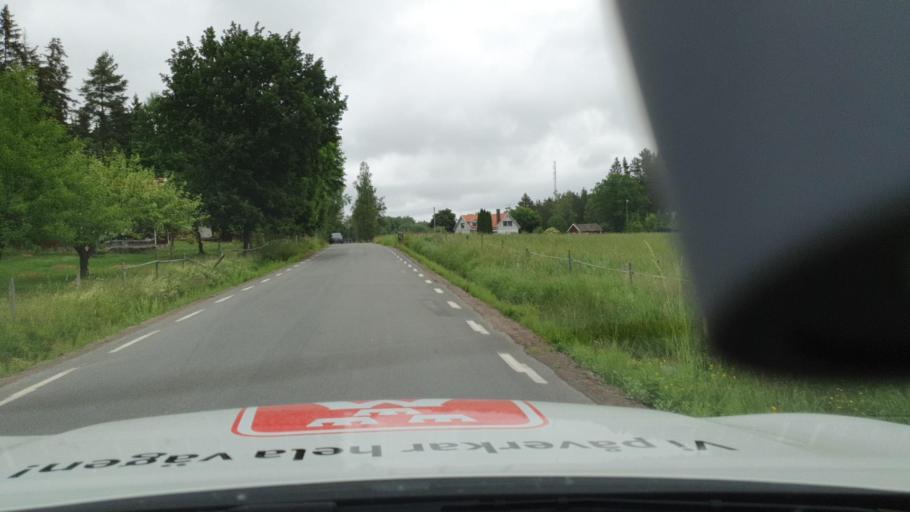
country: SE
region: Vaestra Goetaland
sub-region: Tibro Kommun
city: Tibro
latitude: 58.4116
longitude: 14.0665
